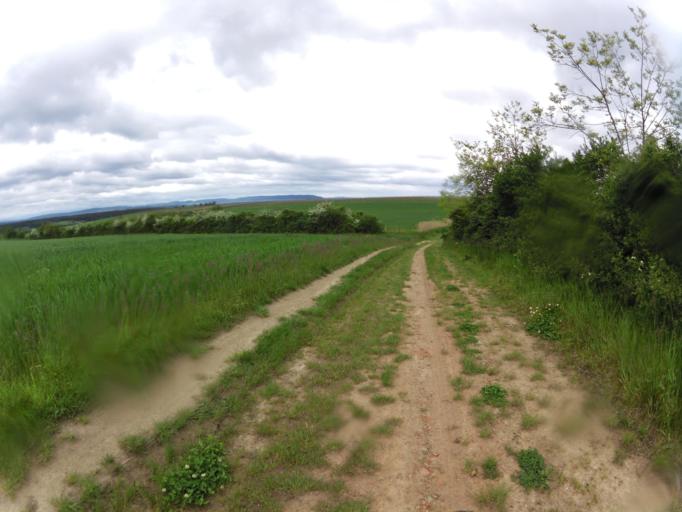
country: DE
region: Bavaria
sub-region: Regierungsbezirk Unterfranken
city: Sommerach
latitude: 49.8450
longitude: 10.2108
